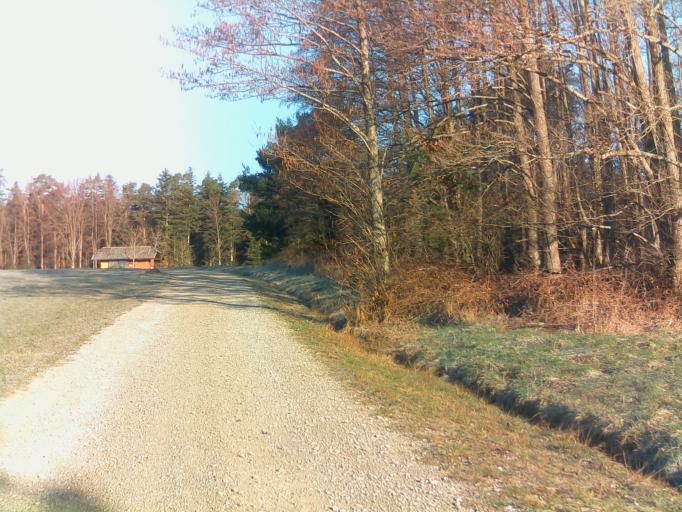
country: DE
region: Baden-Wuerttemberg
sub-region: Karlsruhe Region
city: Oberreichenbach
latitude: 48.7381
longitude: 8.6574
